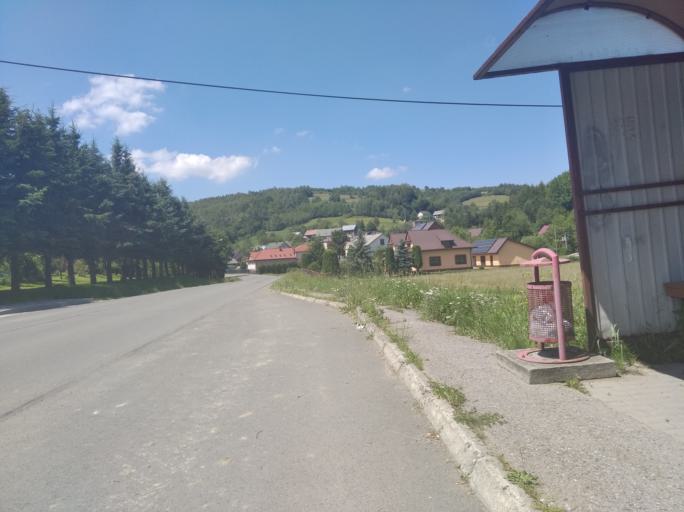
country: PL
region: Subcarpathian Voivodeship
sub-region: Powiat brzozowski
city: Jablonka
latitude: 49.6992
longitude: 22.1241
